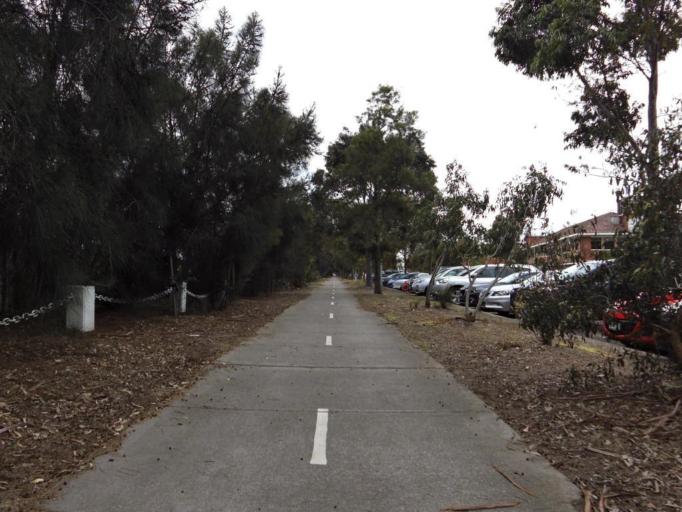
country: AU
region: Victoria
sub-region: Maribyrnong
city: Yarraville
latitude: -37.8293
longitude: 144.9009
